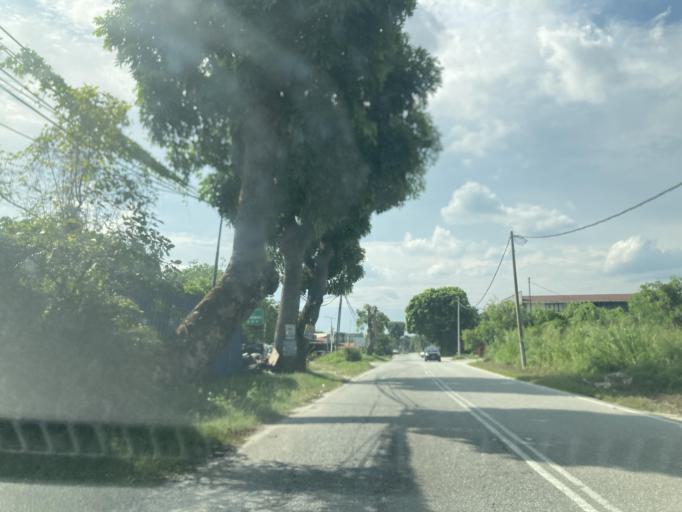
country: MY
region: Selangor
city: Kampung Baru Subang
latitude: 3.1431
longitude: 101.5452
